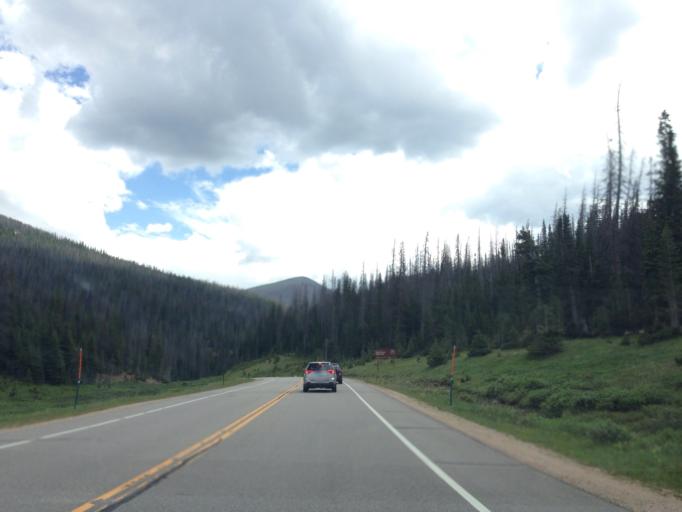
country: US
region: Colorado
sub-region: Larimer County
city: Estes Park
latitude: 40.5166
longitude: -105.8909
